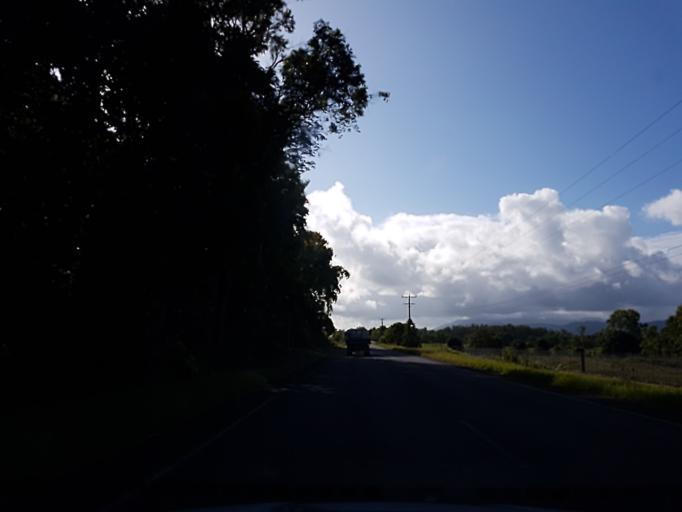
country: AU
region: Queensland
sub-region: Cairns
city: Port Douglas
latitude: -16.3176
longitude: 145.4037
